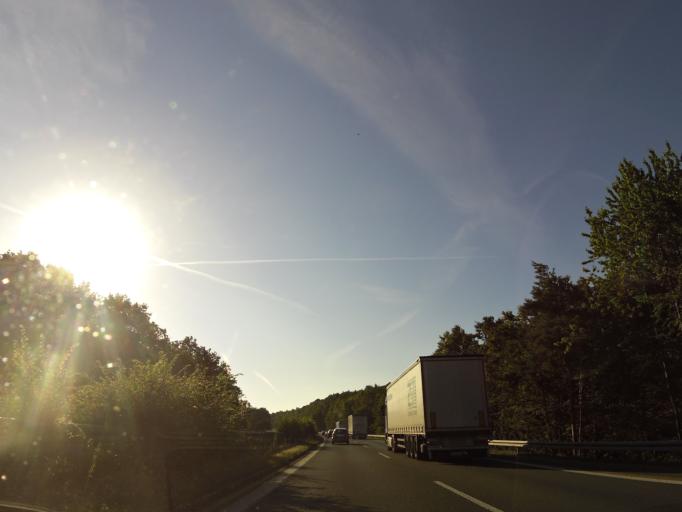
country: DE
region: Bavaria
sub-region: Regierungsbezirk Mittelfranken
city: Vestenbergsgreuth
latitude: 49.7319
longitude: 10.6694
